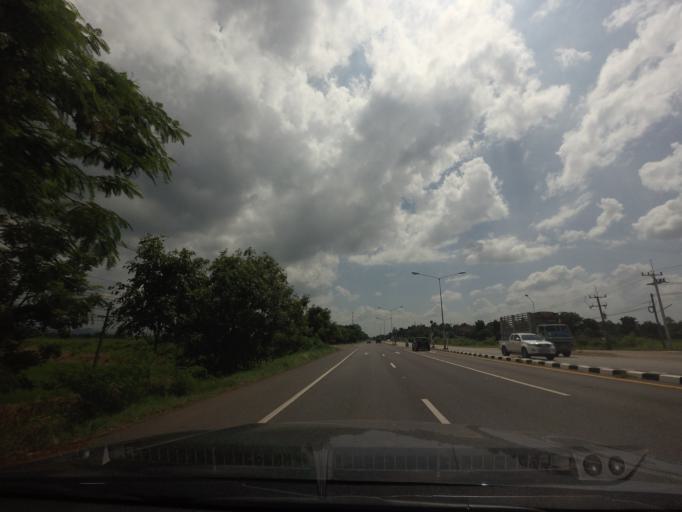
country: TH
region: Phetchabun
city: Nong Phai
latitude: 16.1993
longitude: 101.0890
